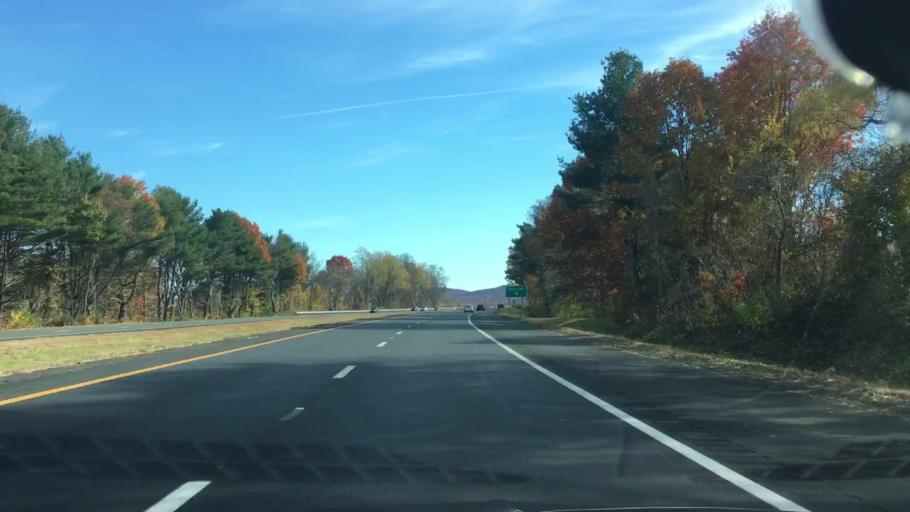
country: US
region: Massachusetts
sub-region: Hampshire County
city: Northampton
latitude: 42.3366
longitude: -72.6277
